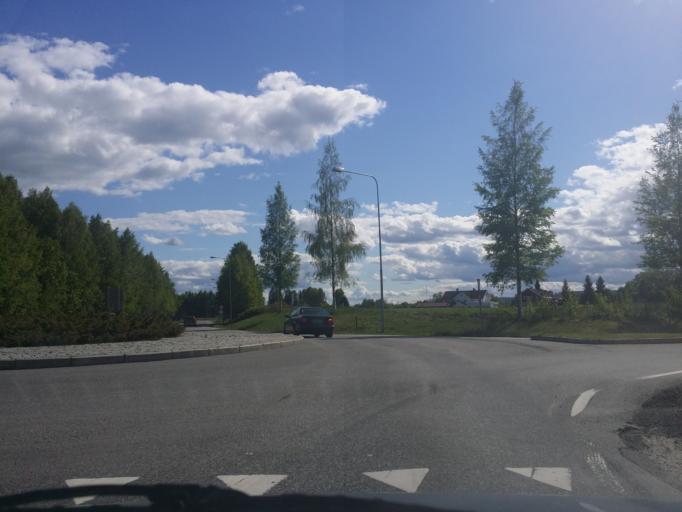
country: NO
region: Akershus
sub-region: Nannestad
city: Teigebyen
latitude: 60.1939
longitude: 11.0662
